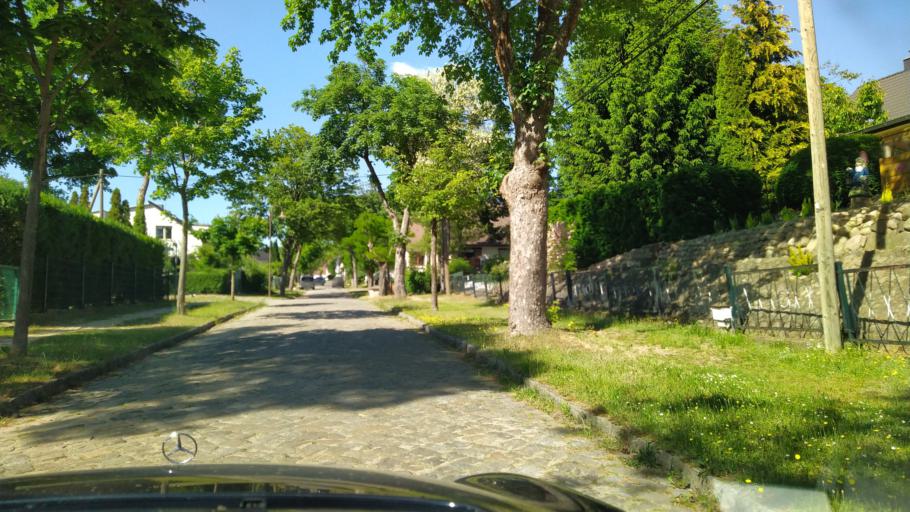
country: DE
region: Brandenburg
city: Trebbin
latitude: 52.2482
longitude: 13.2563
